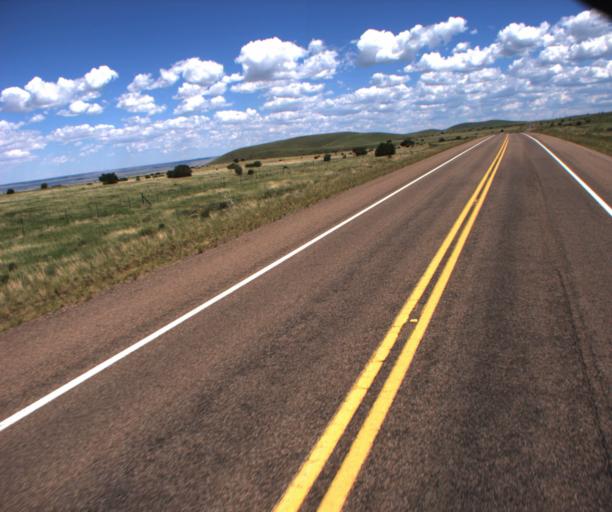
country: US
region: Arizona
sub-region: Apache County
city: Springerville
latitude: 34.2447
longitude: -109.5235
